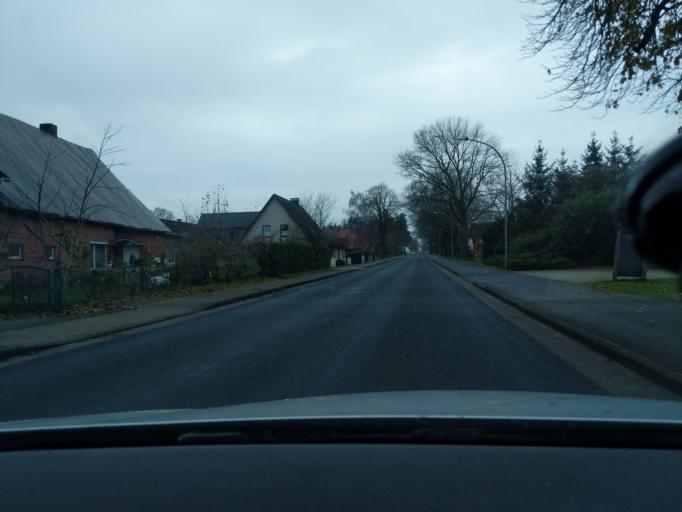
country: DE
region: Lower Saxony
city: Heeslingen
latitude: 53.3457
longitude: 9.3968
